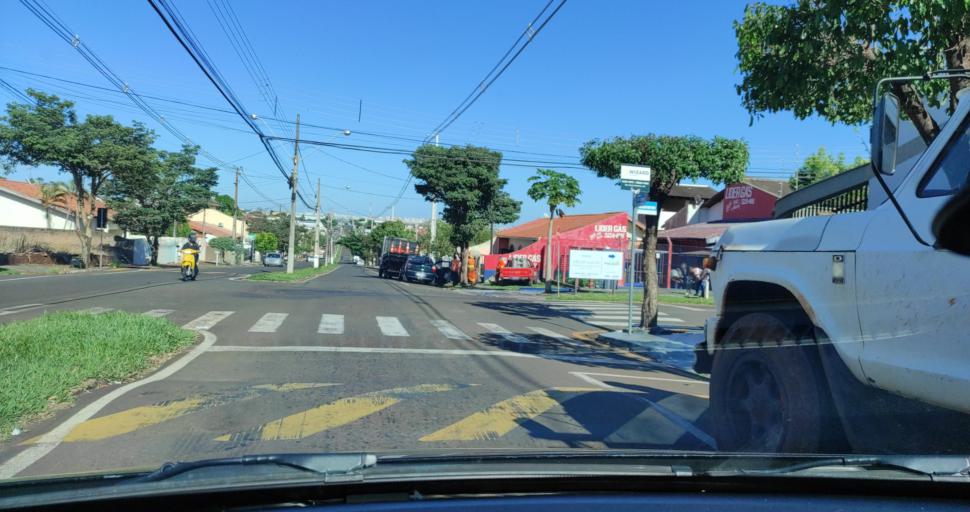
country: BR
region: Parana
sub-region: Ibipora
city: Ibipora
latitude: -23.2726
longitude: -51.0633
